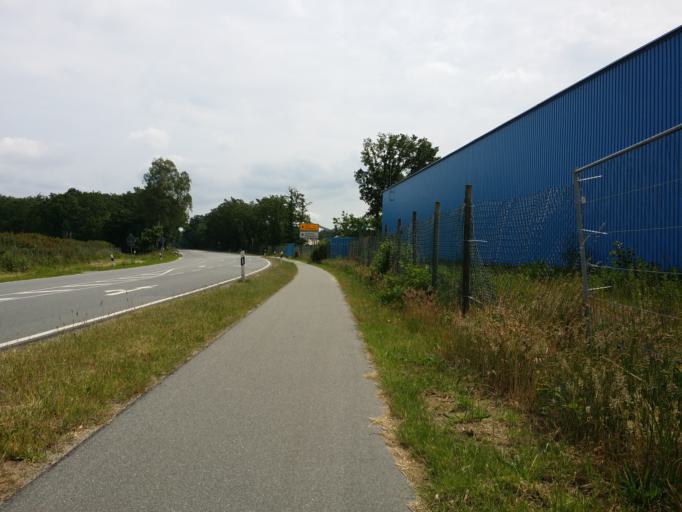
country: DE
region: Lower Saxony
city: Friedeburg
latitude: 53.4085
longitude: 7.8959
